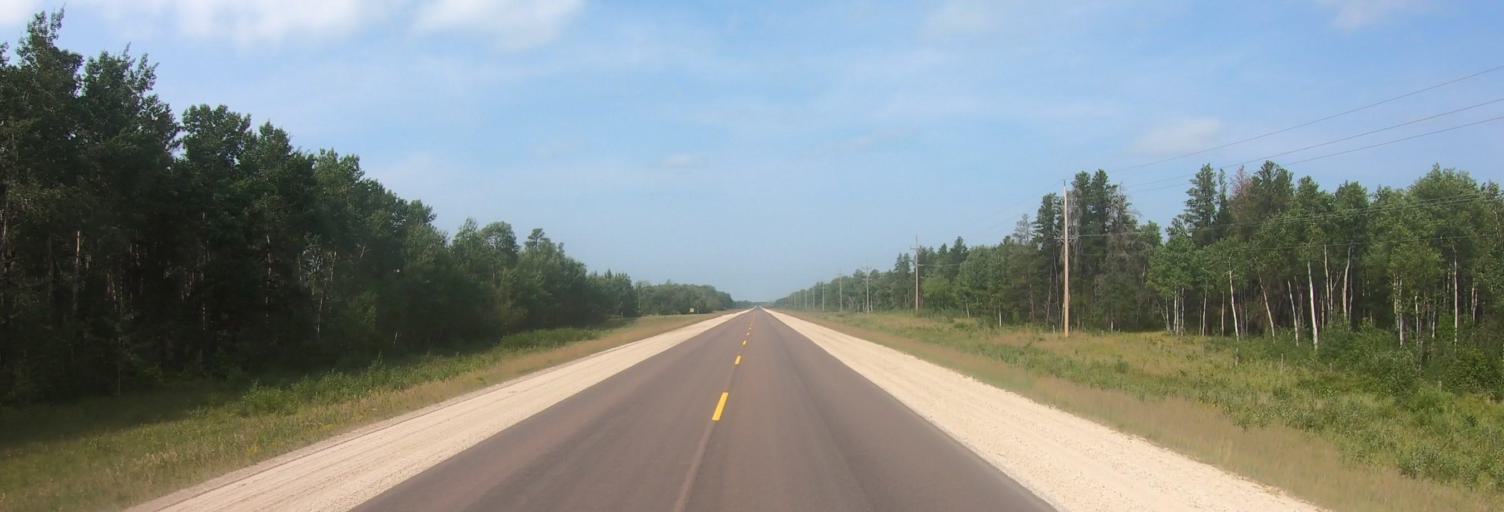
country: CA
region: Manitoba
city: La Broquerie
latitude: 49.2670
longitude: -96.4385
